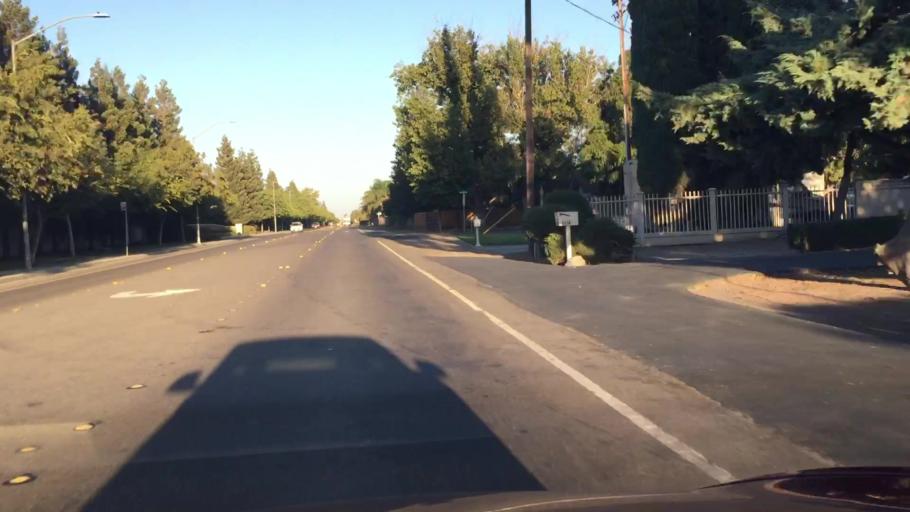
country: US
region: California
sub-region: San Joaquin County
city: Tracy
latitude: 37.7107
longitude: -121.4129
